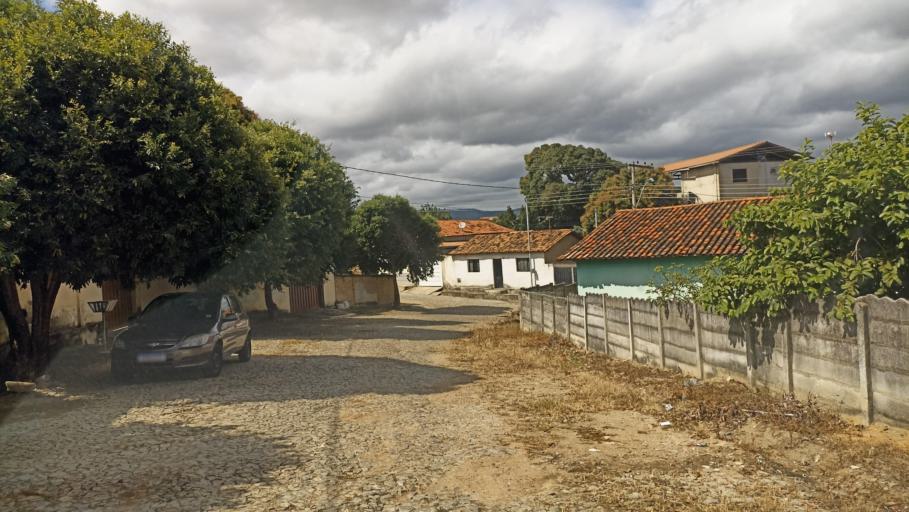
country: BR
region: Minas Gerais
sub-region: Jequitinhonha
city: Jequitinhonha
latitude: -16.4366
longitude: -41.0112
